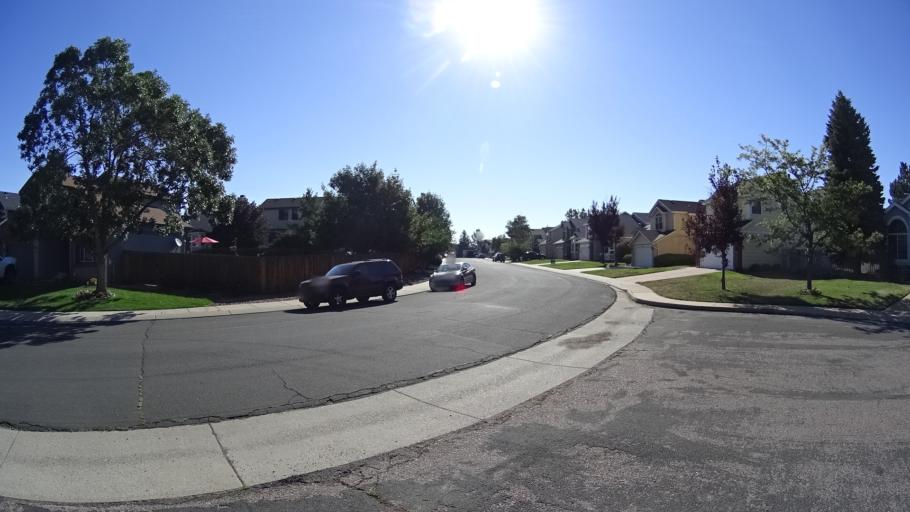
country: US
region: Colorado
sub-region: El Paso County
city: Black Forest
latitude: 38.9582
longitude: -104.7602
